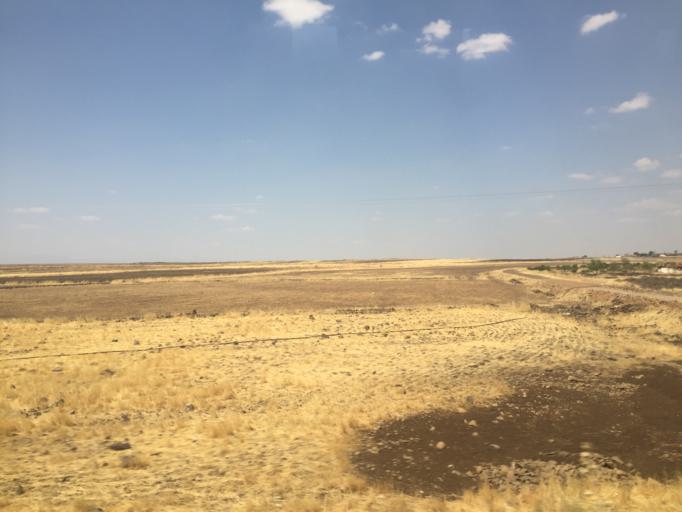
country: TR
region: Sanliurfa
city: Siverek
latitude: 37.7717
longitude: 39.4430
